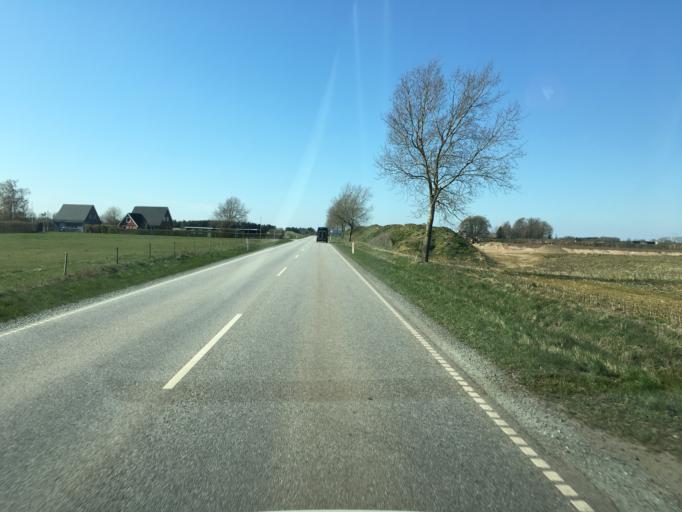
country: DK
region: South Denmark
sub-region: Aabenraa Kommune
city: Tinglev
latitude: 54.9680
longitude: 9.3157
